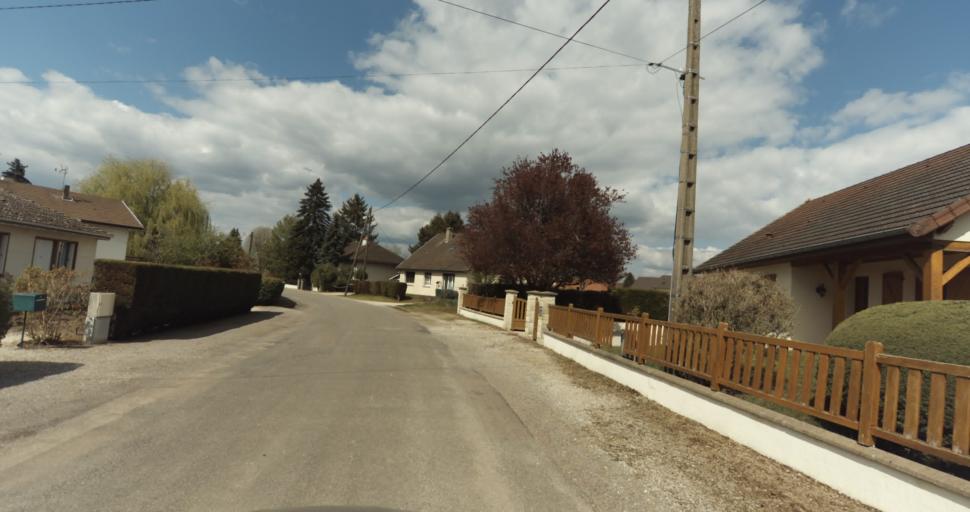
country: FR
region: Bourgogne
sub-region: Departement de la Cote-d'Or
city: Auxonne
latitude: 47.1824
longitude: 5.3965
